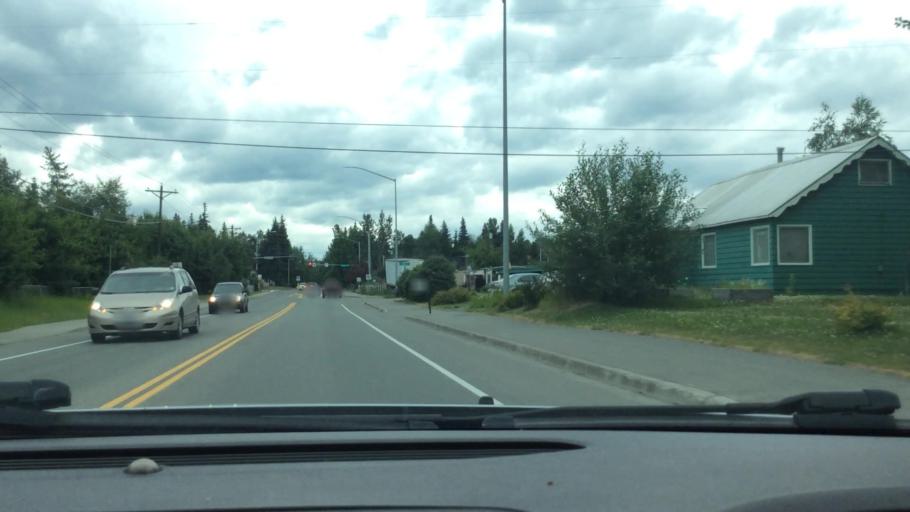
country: US
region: Alaska
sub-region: Anchorage Municipality
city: Elmendorf Air Force Base
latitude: 61.2115
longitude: -149.7560
